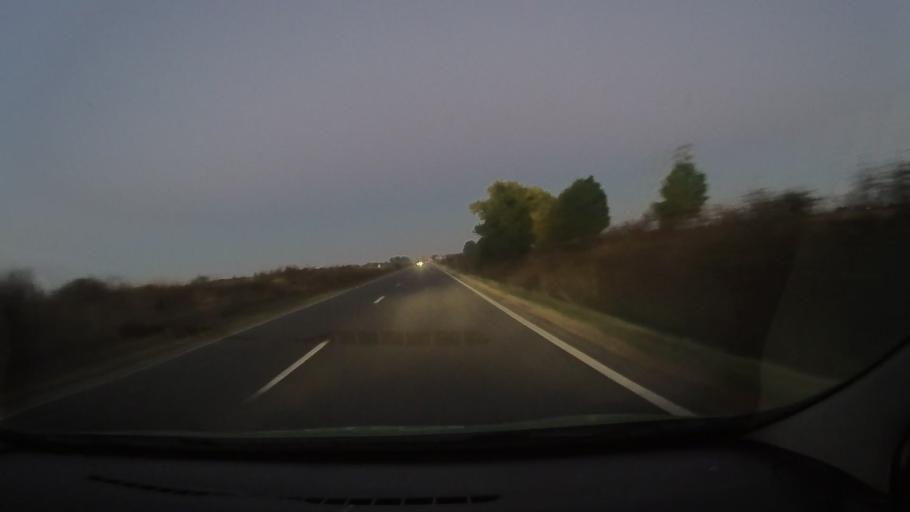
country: RO
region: Bihor
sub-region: Comuna Simian
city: Simian
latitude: 47.5091
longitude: 22.1040
